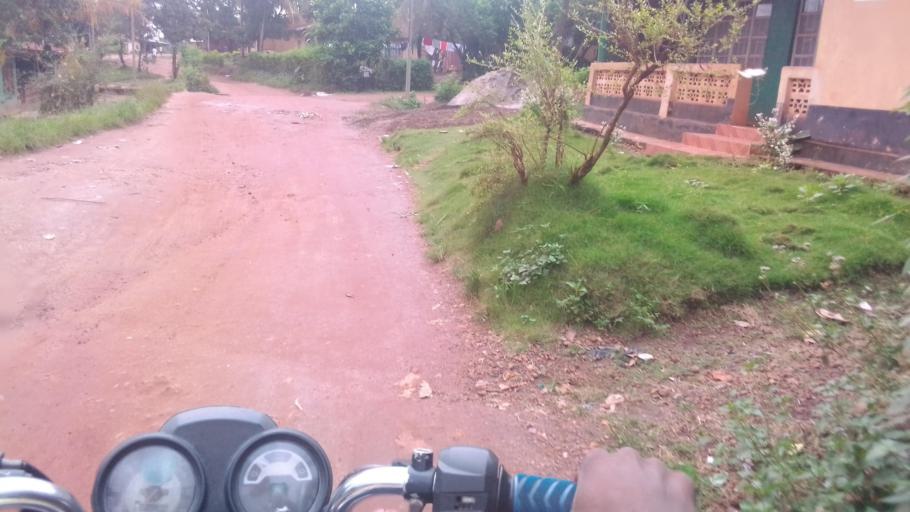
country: SL
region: Eastern Province
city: Kenema
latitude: 7.8706
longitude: -11.1783
